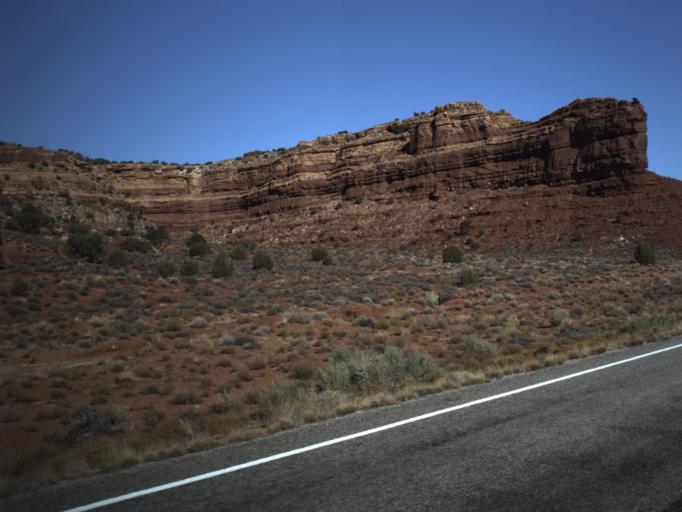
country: US
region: Utah
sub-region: San Juan County
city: Blanding
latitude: 37.7176
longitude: -110.2462
